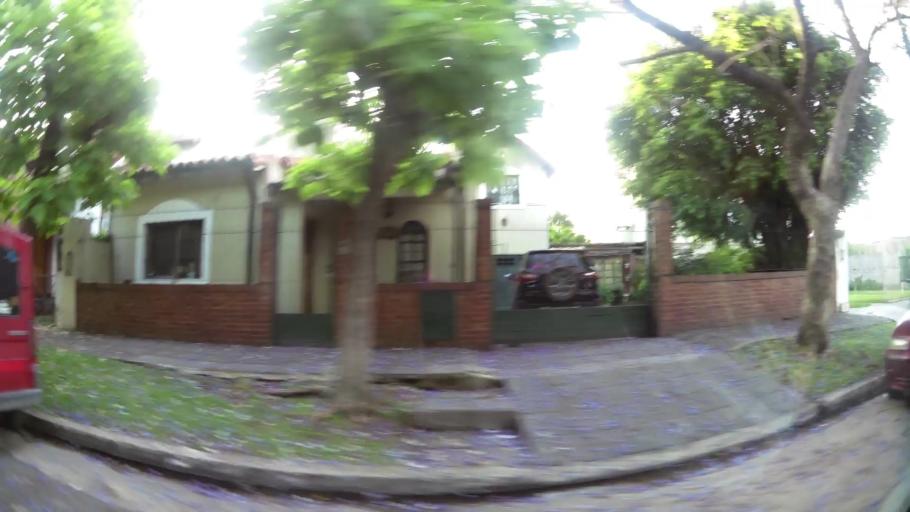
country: AR
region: Buenos Aires
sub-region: Partido de Moron
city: Moron
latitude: -34.6439
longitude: -58.6325
